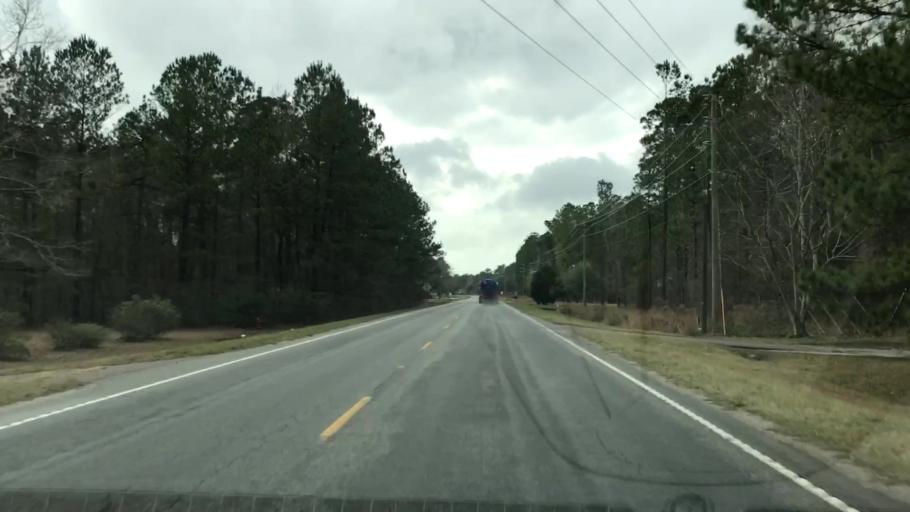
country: US
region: South Carolina
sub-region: Berkeley County
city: Saint Stephen
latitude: 33.2862
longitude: -79.8577
